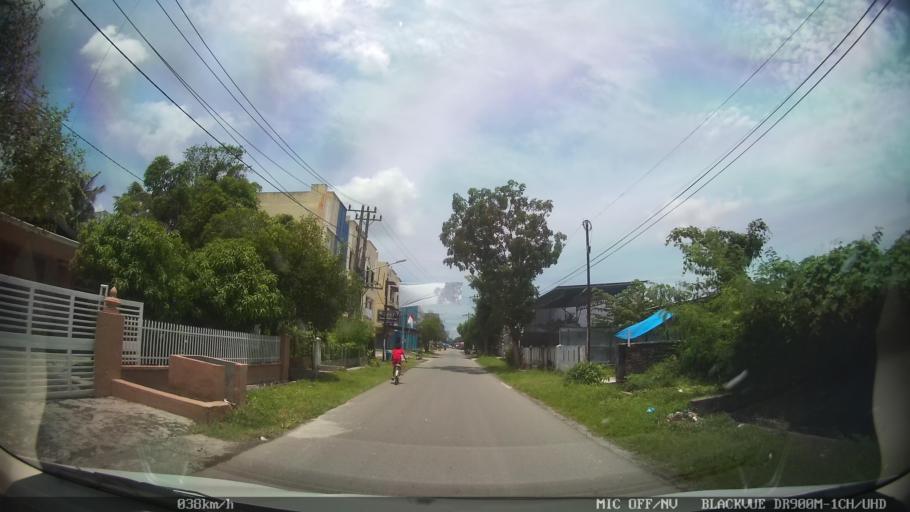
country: ID
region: North Sumatra
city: Percut
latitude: 3.5575
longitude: 98.8713
